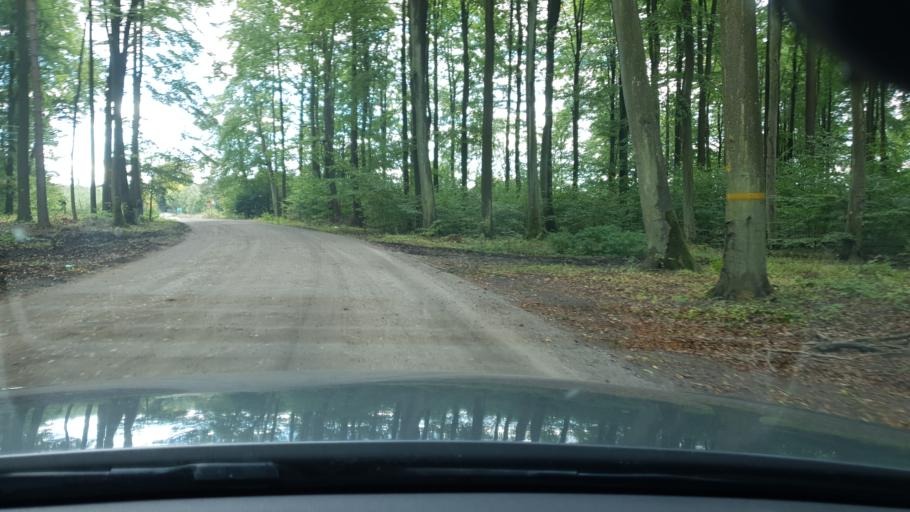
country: PL
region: Pomeranian Voivodeship
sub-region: Powiat wejherowski
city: Reda
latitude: 54.5826
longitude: 18.3135
